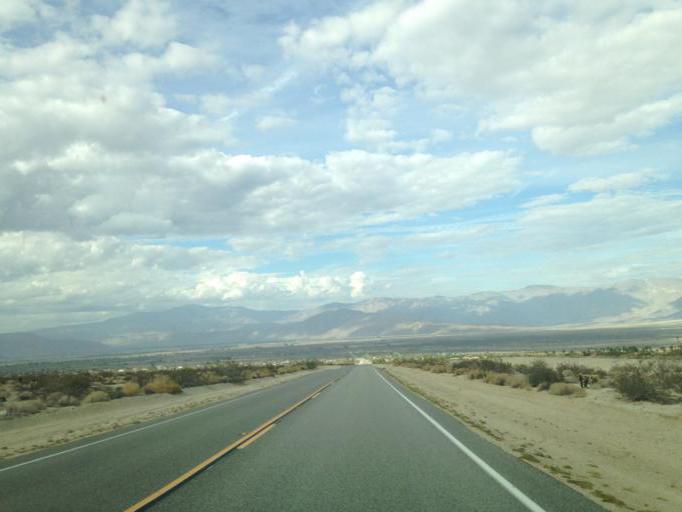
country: US
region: California
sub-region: San Diego County
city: Borrego Springs
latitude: 33.1860
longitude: -116.3308
